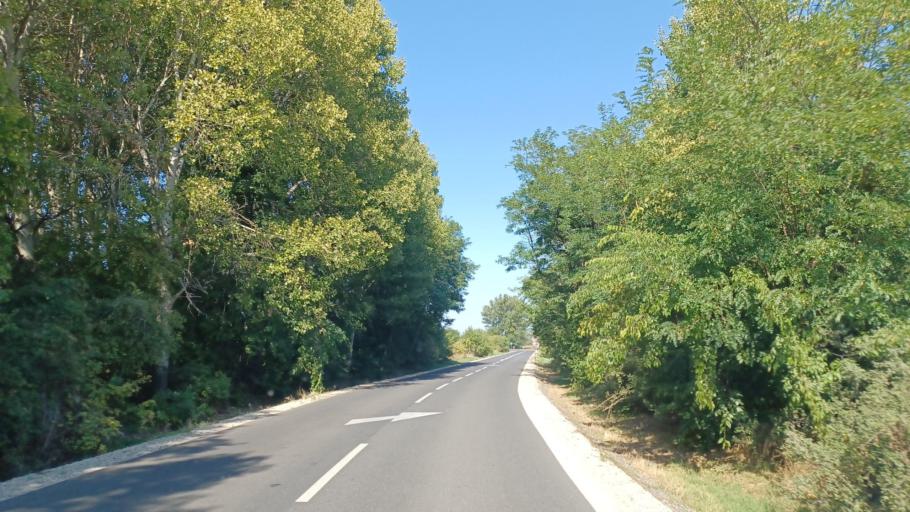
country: HU
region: Fejer
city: Alap
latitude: 46.7479
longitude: 18.6855
